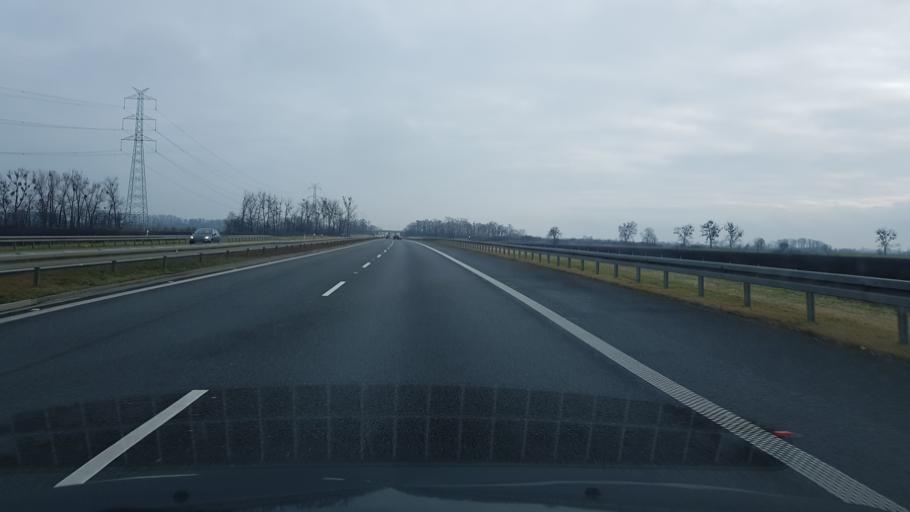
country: PL
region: Lower Silesian Voivodeship
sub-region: Powiat olawski
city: Wierzbno
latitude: 50.9148
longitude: 17.1442
